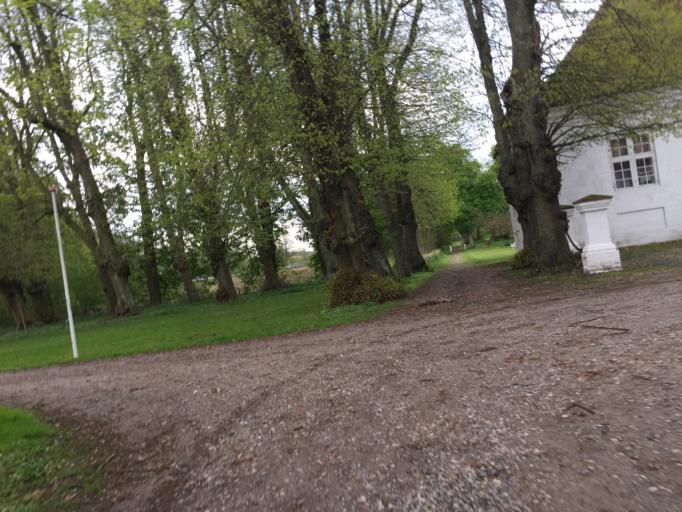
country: DK
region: North Denmark
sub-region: Alborg Kommune
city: Frejlev
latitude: 57.0051
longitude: 9.7754
